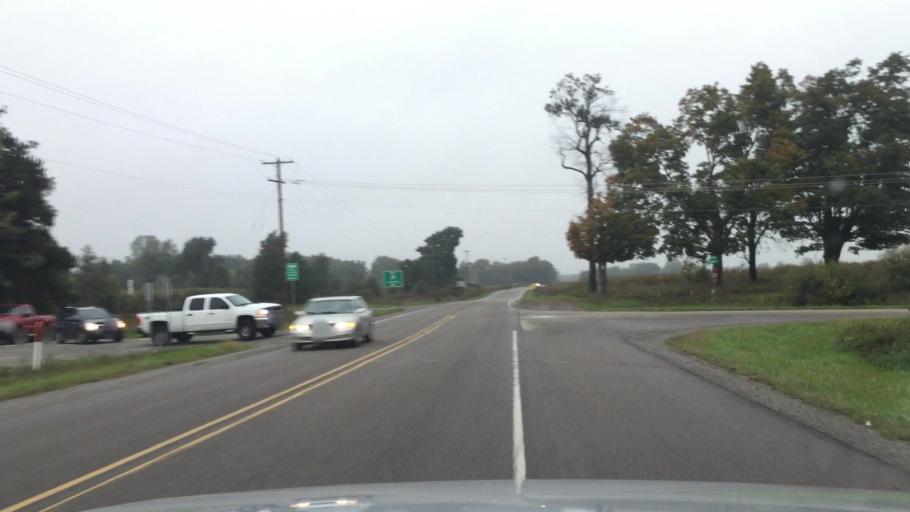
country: US
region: Michigan
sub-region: Shiawassee County
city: Corunna
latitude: 42.8954
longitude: -84.0954
